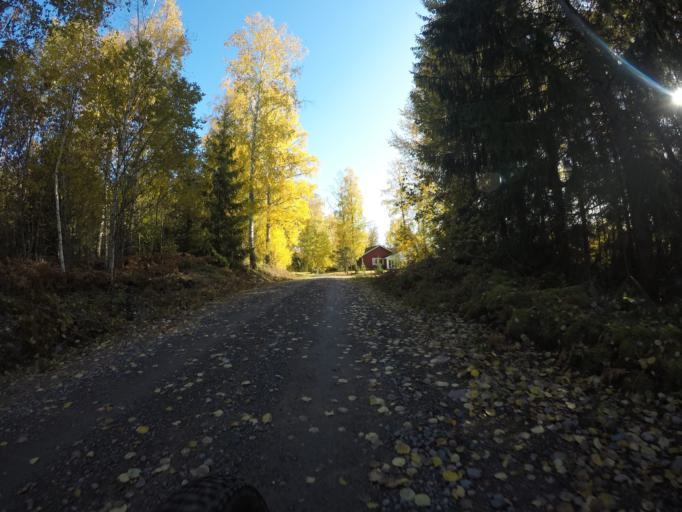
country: SE
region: Vaestmanland
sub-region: Kungsors Kommun
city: Kungsoer
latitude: 59.3169
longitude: 16.0966
